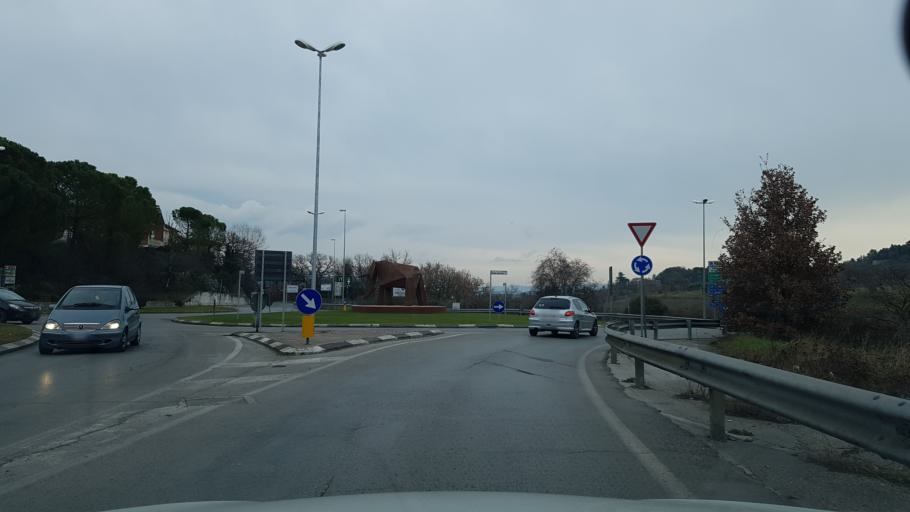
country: IT
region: Umbria
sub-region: Provincia di Perugia
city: Lacugnano
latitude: 43.1034
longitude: 12.3459
